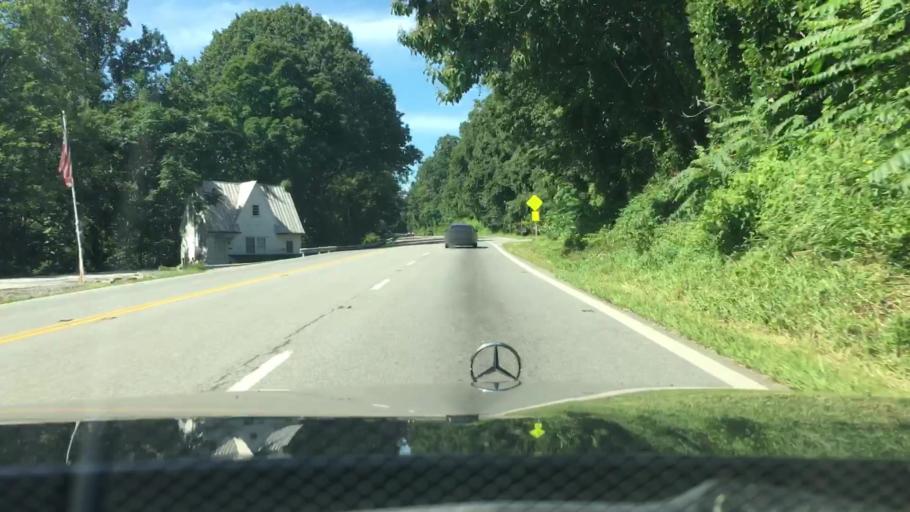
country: US
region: Virginia
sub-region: City of Waynesboro
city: Waynesboro
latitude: 38.0368
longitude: -78.8399
